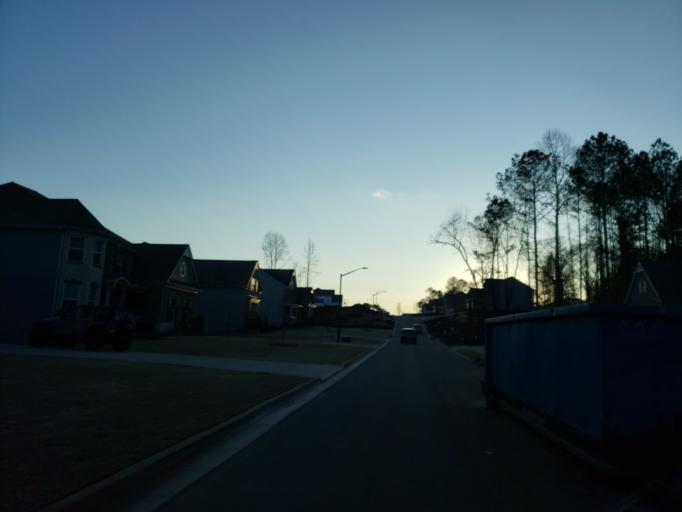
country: US
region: Georgia
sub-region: Cherokee County
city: Woodstock
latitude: 34.1189
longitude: -84.4516
